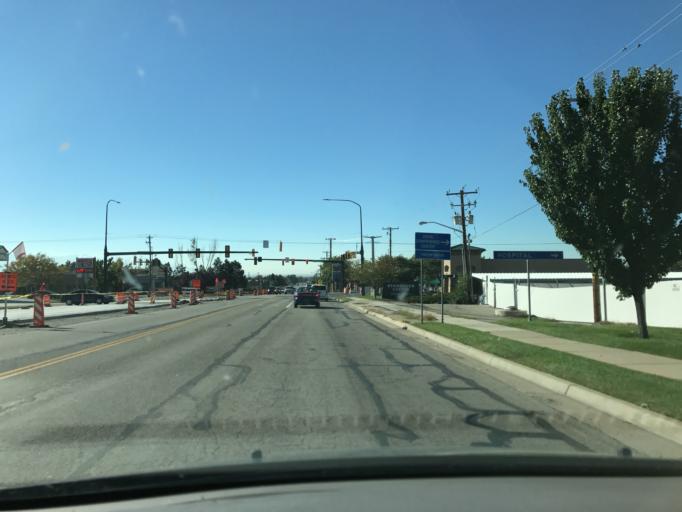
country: US
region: Utah
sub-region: Davis County
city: Hill Air Force Bace
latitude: 41.0901
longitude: -111.9736
